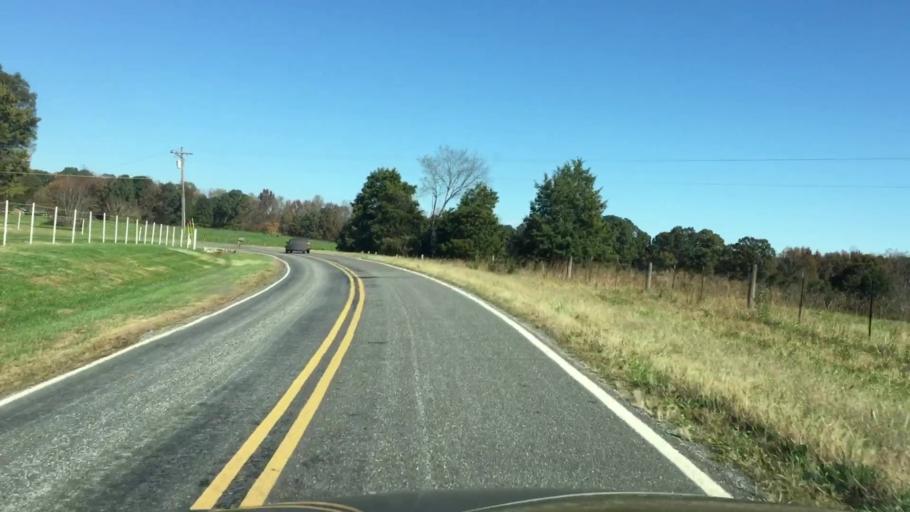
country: US
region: North Carolina
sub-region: Iredell County
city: Mooresville
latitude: 35.5752
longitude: -80.7621
